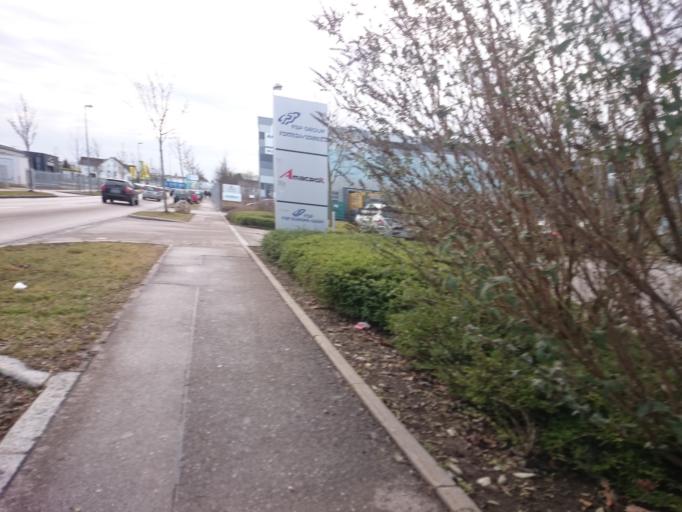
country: DE
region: Bavaria
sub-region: Swabia
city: Konigsbrunn
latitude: 48.3226
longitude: 10.8949
